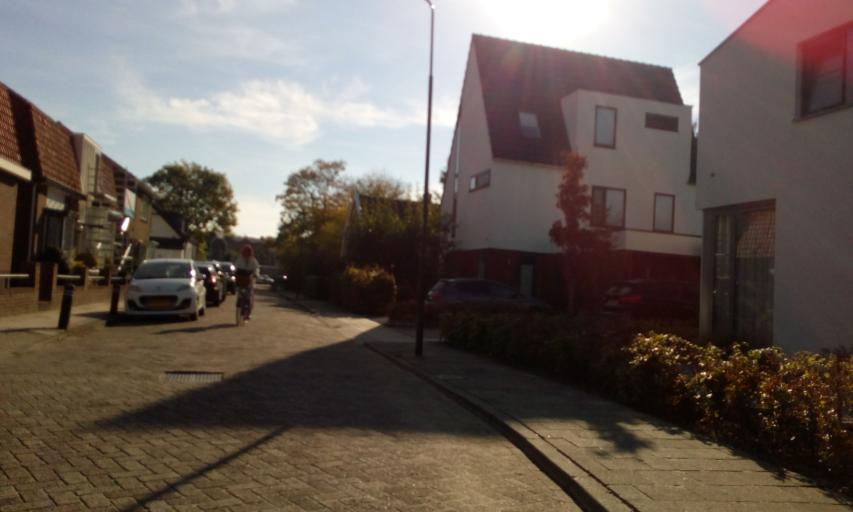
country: NL
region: Utrecht
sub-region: Stichtse Vecht
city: Spechtenkamp
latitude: 52.1059
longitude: 5.0101
